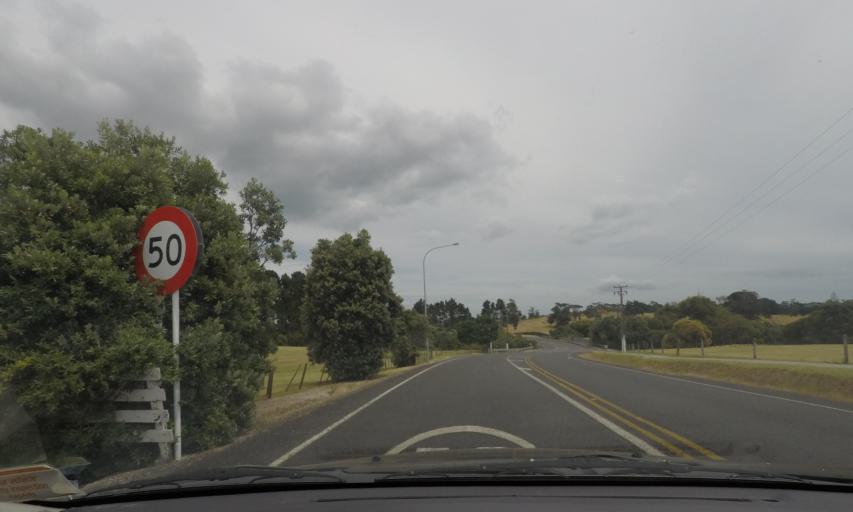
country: NZ
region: Auckland
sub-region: Auckland
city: Mangere
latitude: -36.9785
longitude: 174.7639
